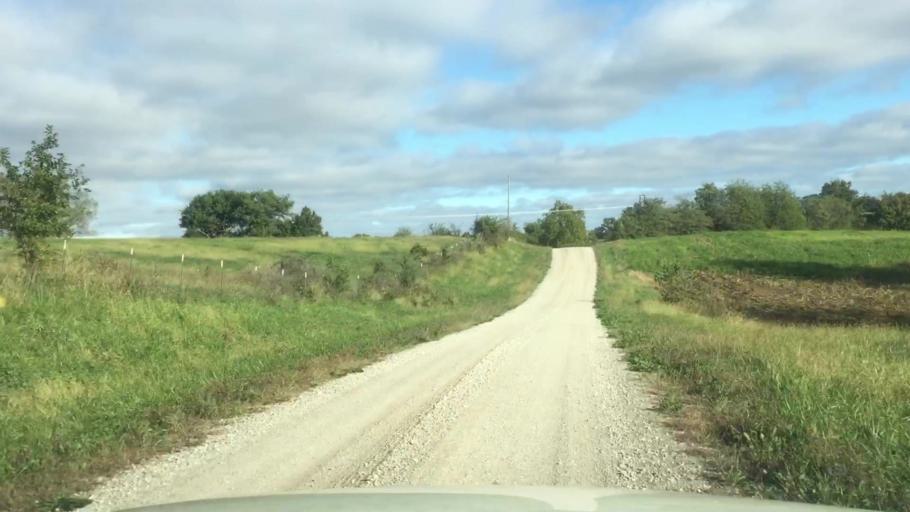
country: US
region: Missouri
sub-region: Howard County
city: New Franklin
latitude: 39.0985
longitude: -92.7794
